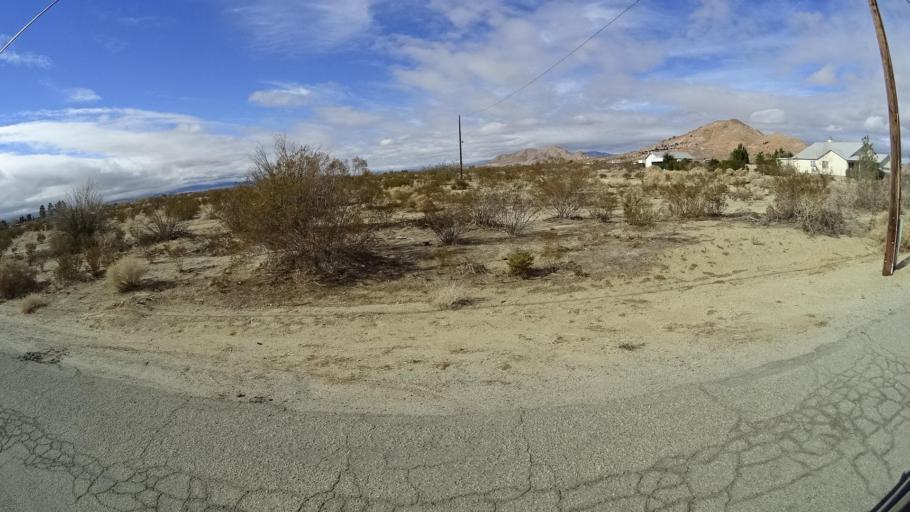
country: US
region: California
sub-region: Kern County
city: Rosamond
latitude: 34.8724
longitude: -118.2202
